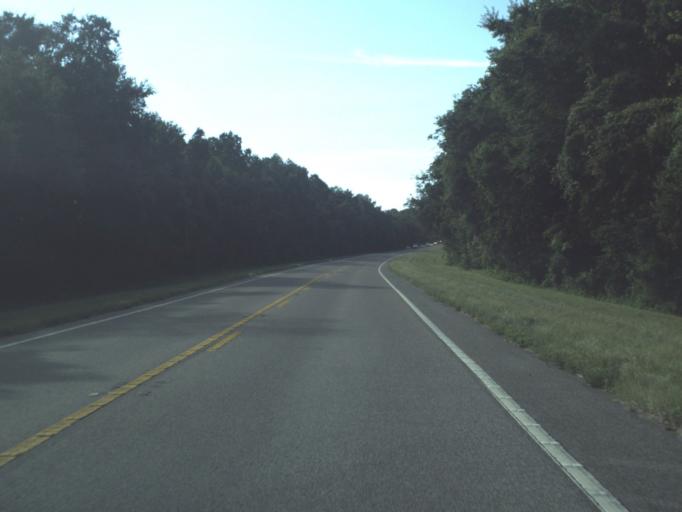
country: US
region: Florida
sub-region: Hernando County
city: North Brooksville
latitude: 28.6442
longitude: -82.4373
